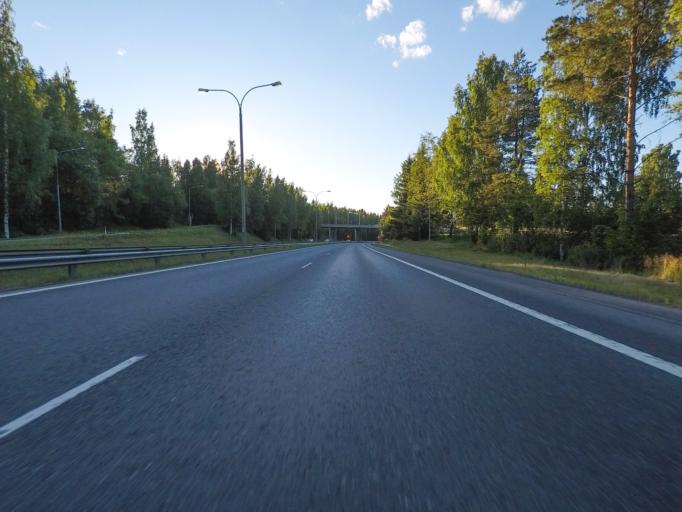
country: FI
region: Northern Savo
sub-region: Kuopio
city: Kuopio
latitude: 62.9315
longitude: 27.6724
